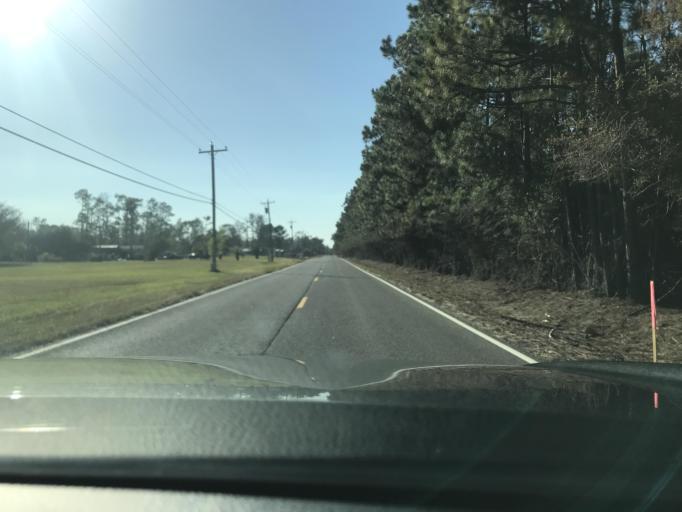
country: US
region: Louisiana
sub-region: Calcasieu Parish
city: Moss Bluff
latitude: 30.3225
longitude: -93.2708
